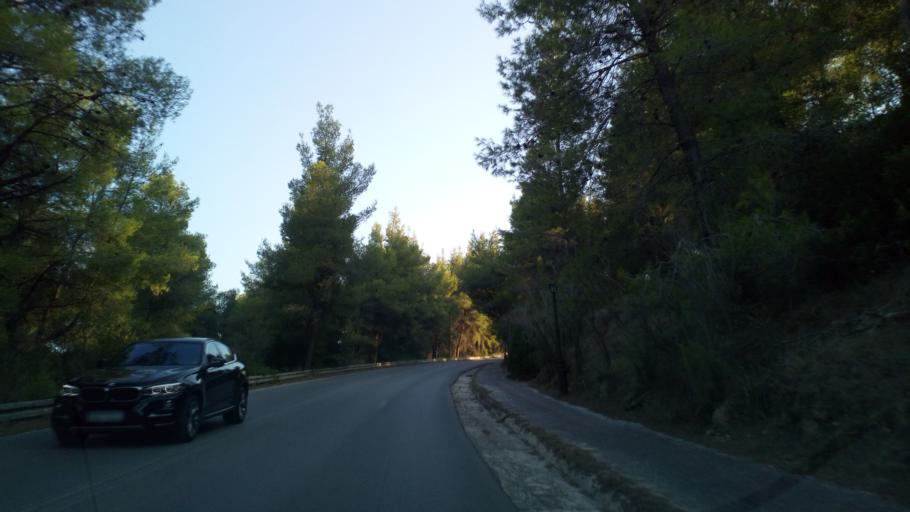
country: GR
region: Central Macedonia
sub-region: Nomos Chalkidikis
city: Pefkochori
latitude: 39.9478
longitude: 23.6740
